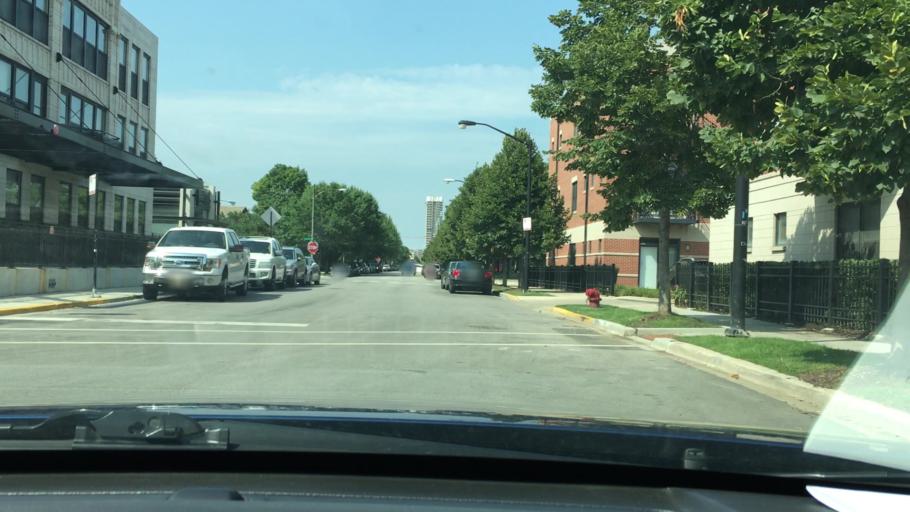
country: US
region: Illinois
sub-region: Cook County
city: Chicago
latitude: 41.8617
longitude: -87.6508
